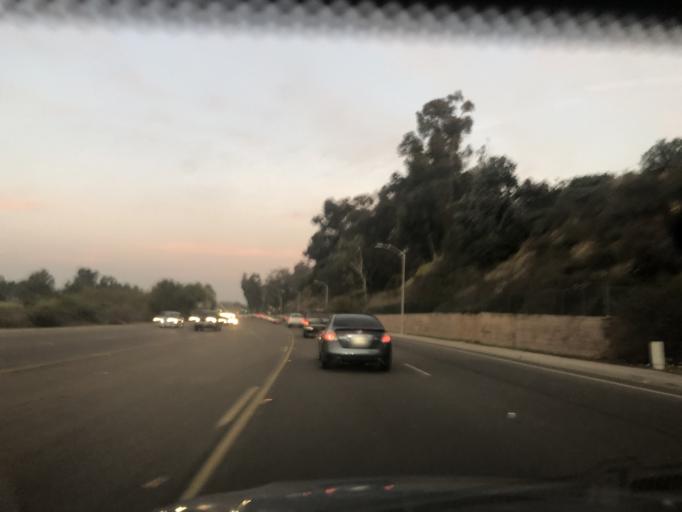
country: US
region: California
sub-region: San Diego County
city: Bonita
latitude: 32.6540
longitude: -117.0463
